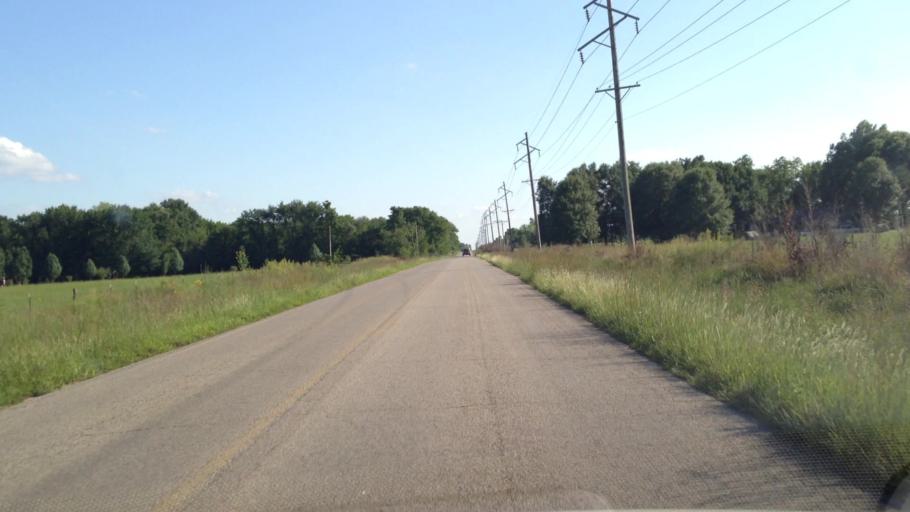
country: US
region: Kansas
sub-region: Crawford County
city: Frontenac
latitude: 37.4679
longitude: -94.6308
